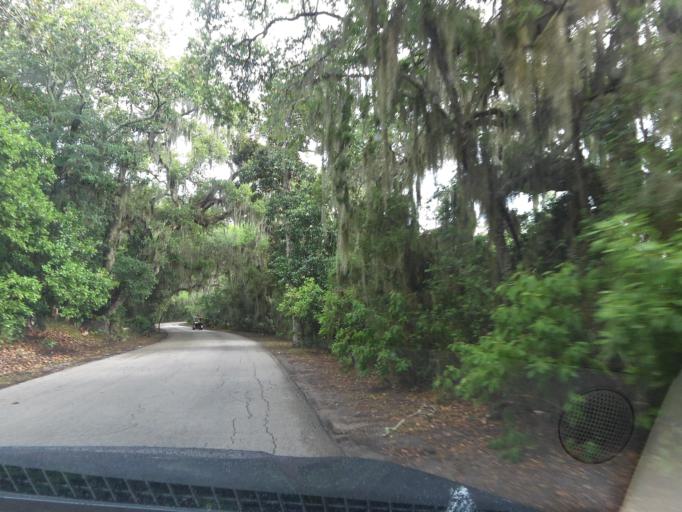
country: US
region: Florida
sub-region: Nassau County
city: Fernandina Beach
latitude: 30.6887
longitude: -81.4386
